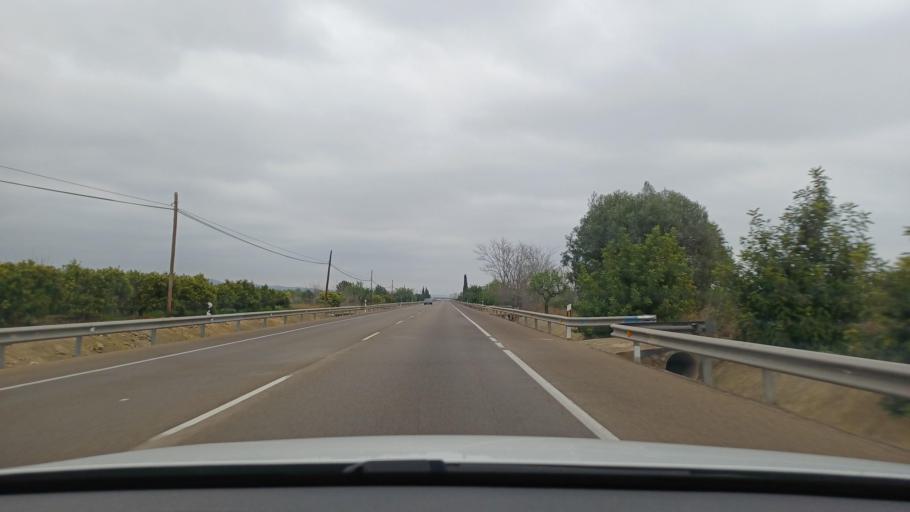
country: ES
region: Valencia
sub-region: Provincia de Castello
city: Orpesa/Oropesa del Mar
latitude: 40.1111
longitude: 0.1388
